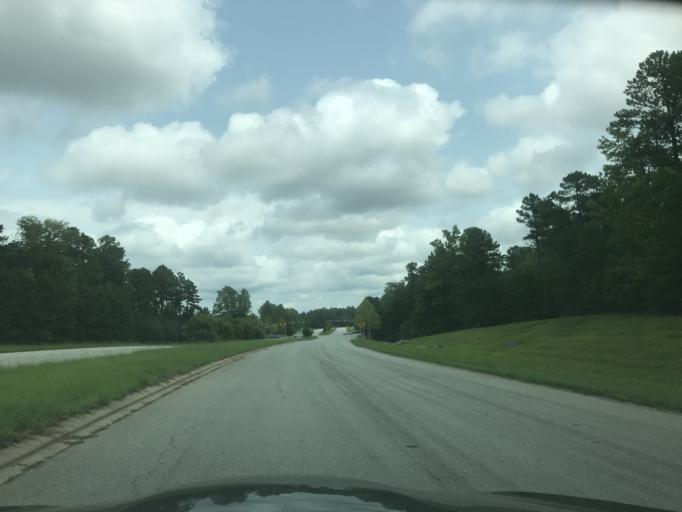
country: US
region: North Carolina
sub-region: Wake County
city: Morrisville
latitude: 35.8578
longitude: -78.8879
